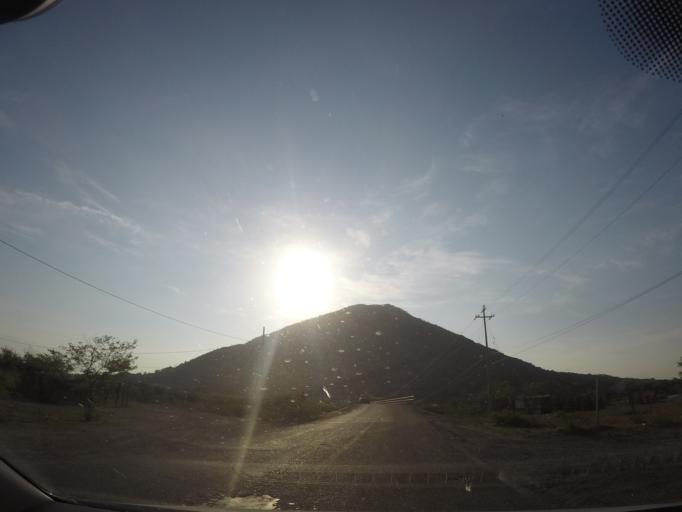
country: MX
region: Oaxaca
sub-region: Santo Domingo Tehuantepec
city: La Noria
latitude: 16.2381
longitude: -95.1574
